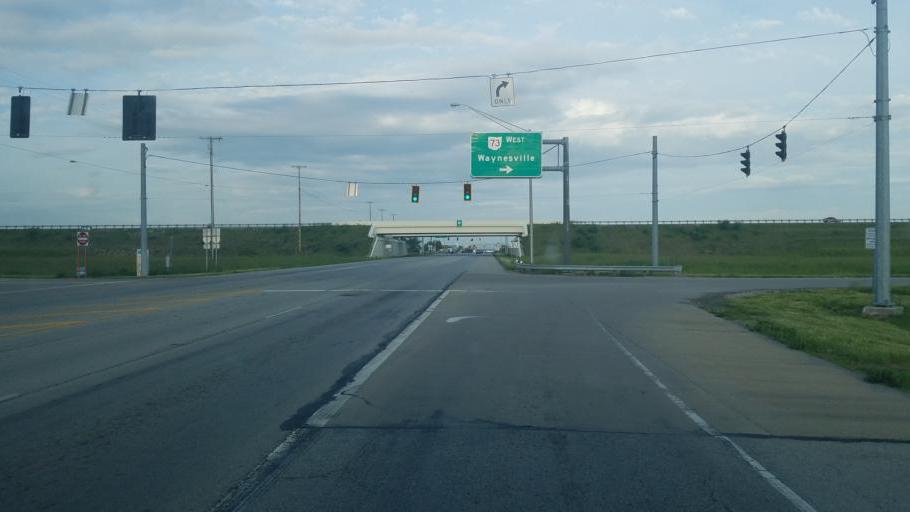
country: US
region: Ohio
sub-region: Clinton County
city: Wilmington
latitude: 39.4565
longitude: -83.7725
